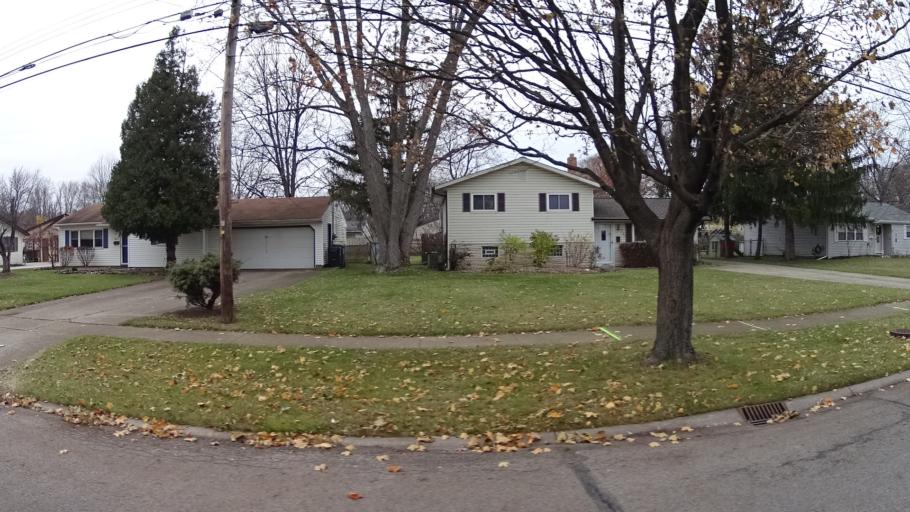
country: US
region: Ohio
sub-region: Lorain County
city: North Ridgeville
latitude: 41.4020
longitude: -82.0052
